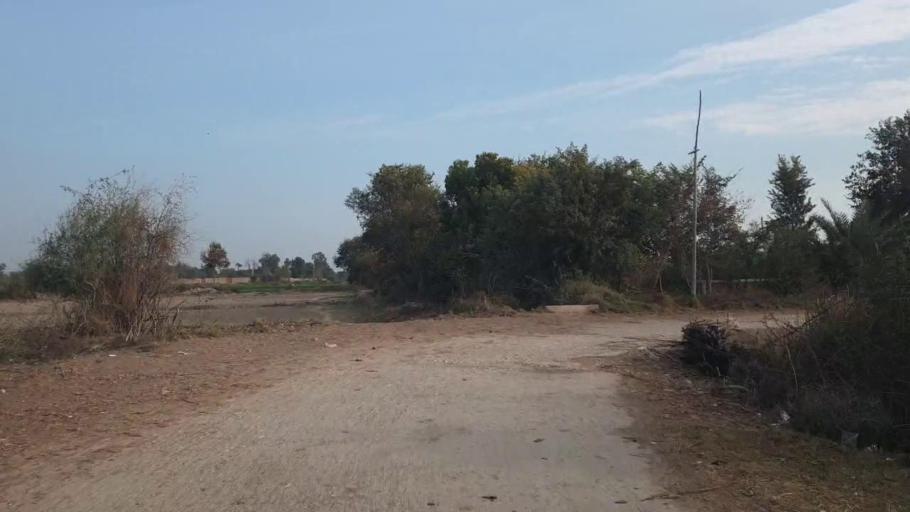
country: PK
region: Sindh
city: Shahpur Chakar
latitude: 26.0535
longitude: 68.5792
